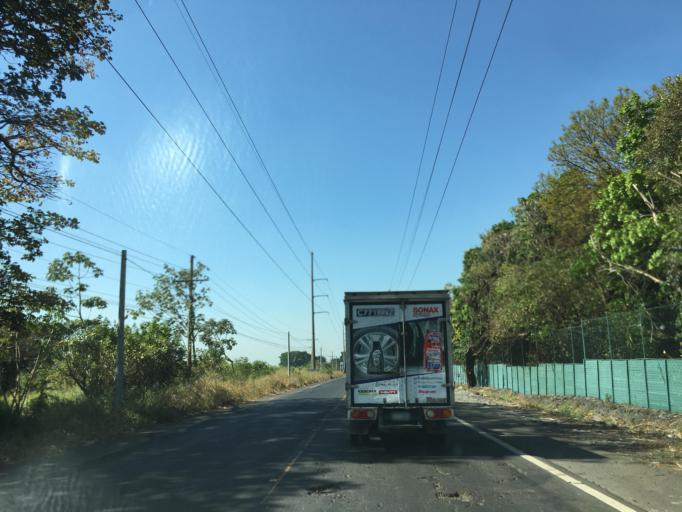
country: GT
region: Escuintla
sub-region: Municipio de Escuintla
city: Escuintla
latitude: 14.2549
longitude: -90.8017
